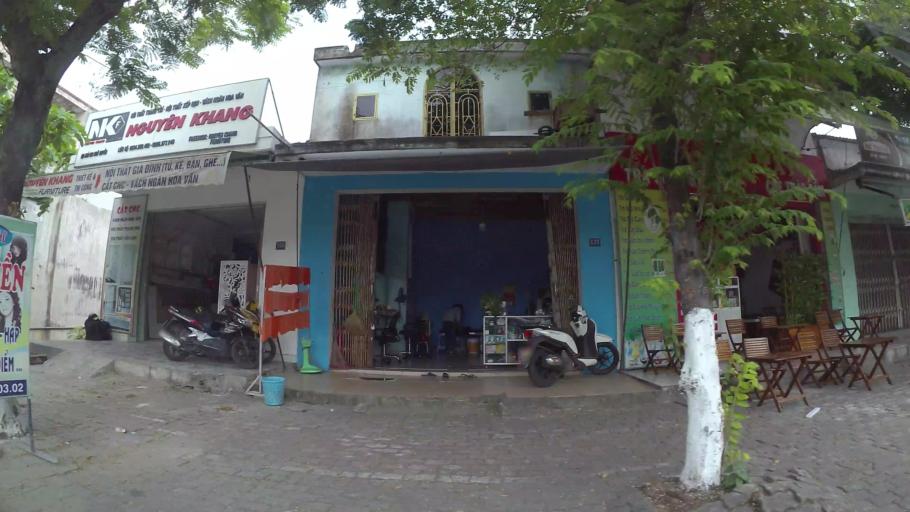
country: VN
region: Da Nang
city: Da Nang
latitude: 16.0946
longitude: 108.2447
